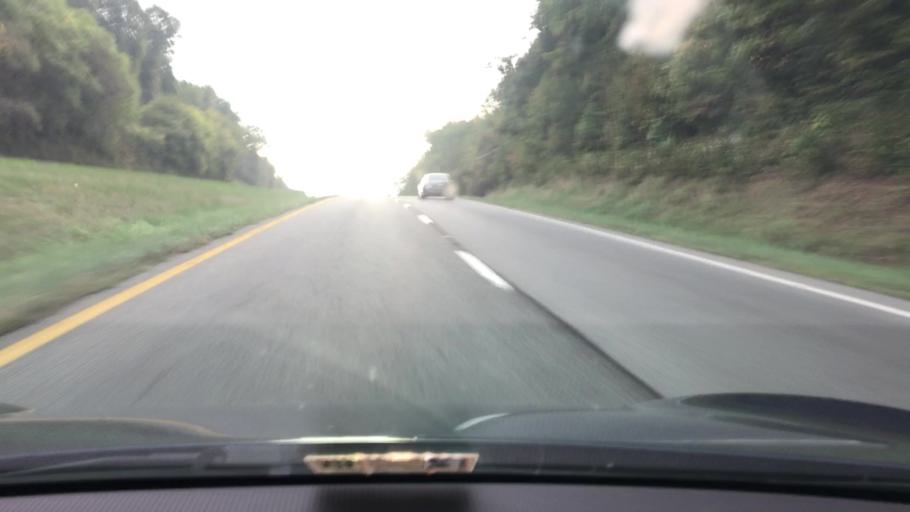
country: US
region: Virginia
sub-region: Botetourt County
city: Blue Ridge
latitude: 37.3965
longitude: -79.7671
